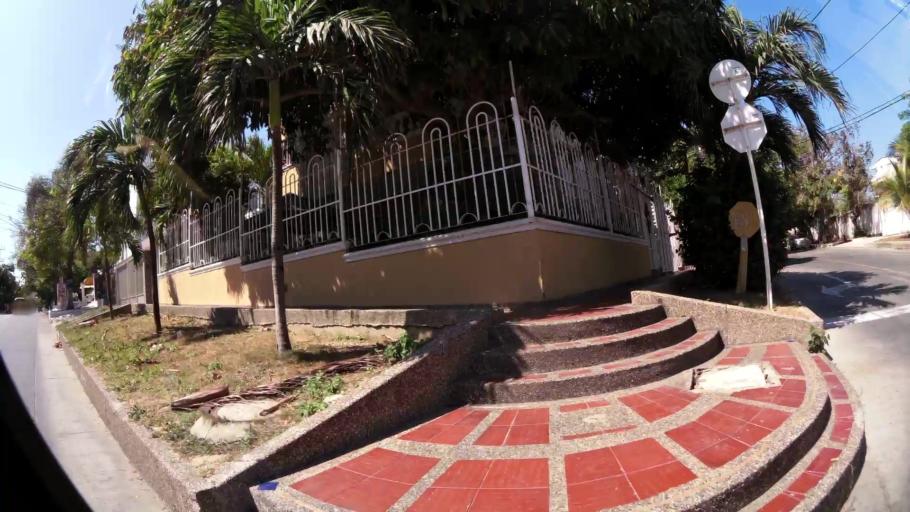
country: CO
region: Atlantico
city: Barranquilla
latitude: 11.0182
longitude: -74.8048
